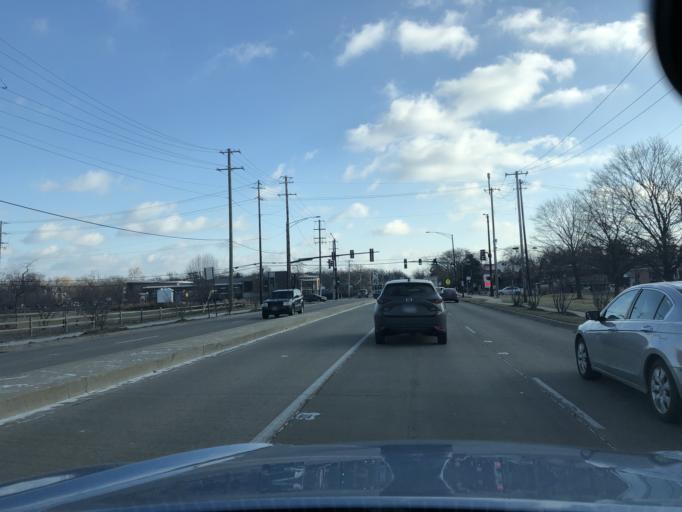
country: US
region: Illinois
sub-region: Cook County
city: Northfield
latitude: 42.1057
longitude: -87.7932
